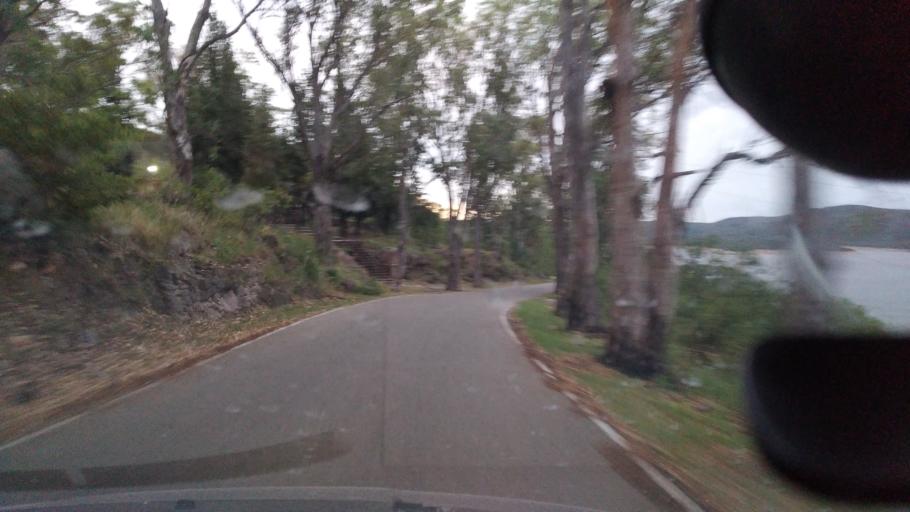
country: AR
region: Cordoba
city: Villa Las Rosas
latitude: -31.8756
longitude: -65.0298
